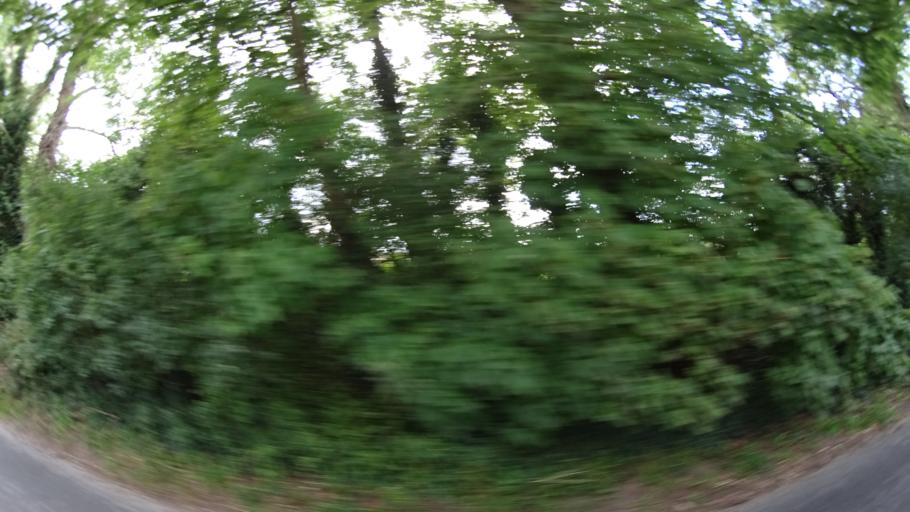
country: GB
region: England
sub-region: Hampshire
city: East Dean
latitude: 51.0855
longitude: -1.5634
